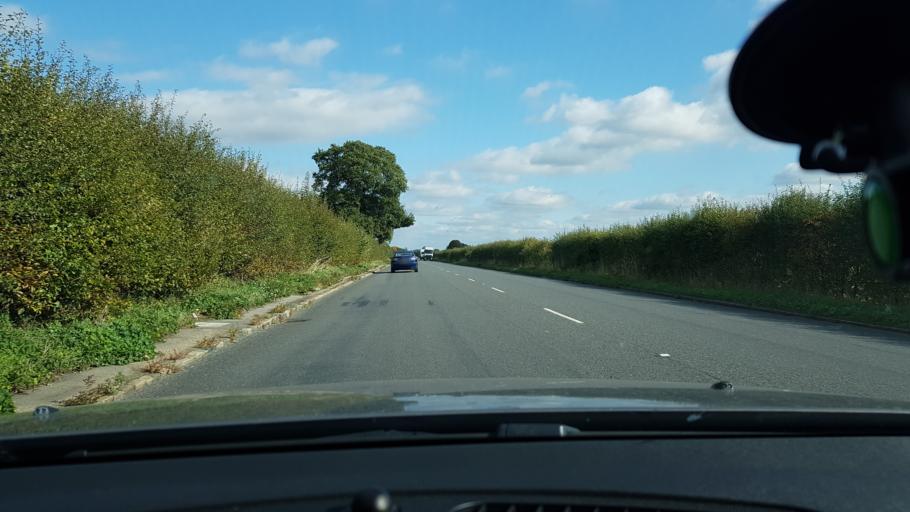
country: GB
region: England
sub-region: West Berkshire
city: Kintbury
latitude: 51.4142
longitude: -1.4728
